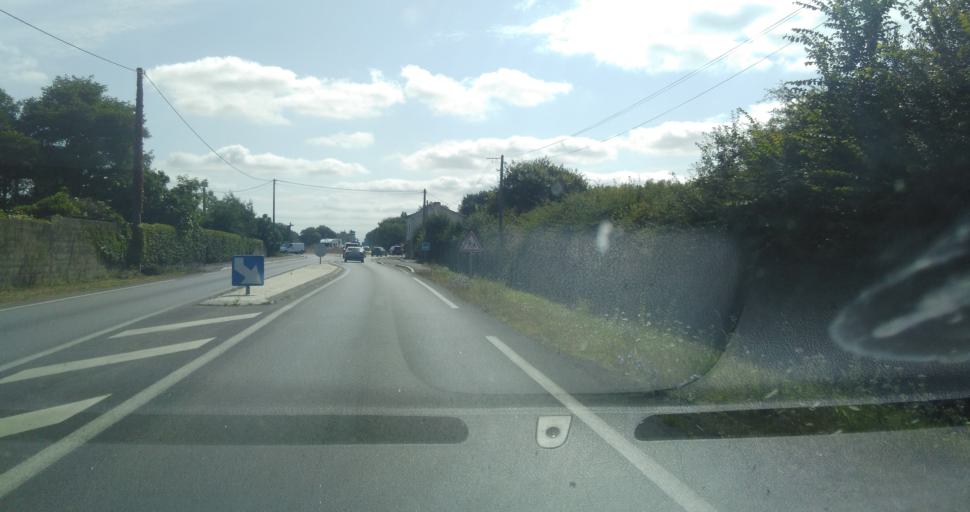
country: FR
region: Pays de la Loire
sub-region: Departement de la Vendee
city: Chateau-d'Olonne
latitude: 46.4789
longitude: -1.6896
